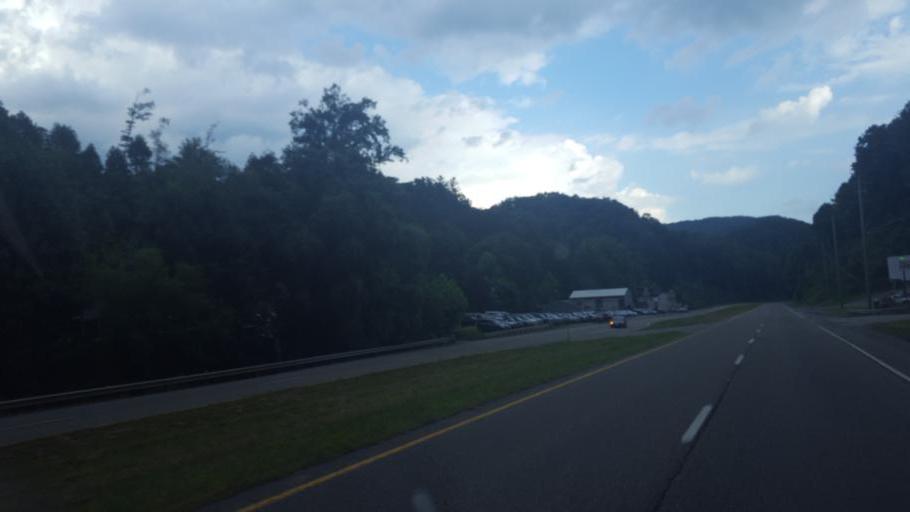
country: US
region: Virginia
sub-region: Wise County
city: Pound
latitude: 37.0581
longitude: -82.6017
